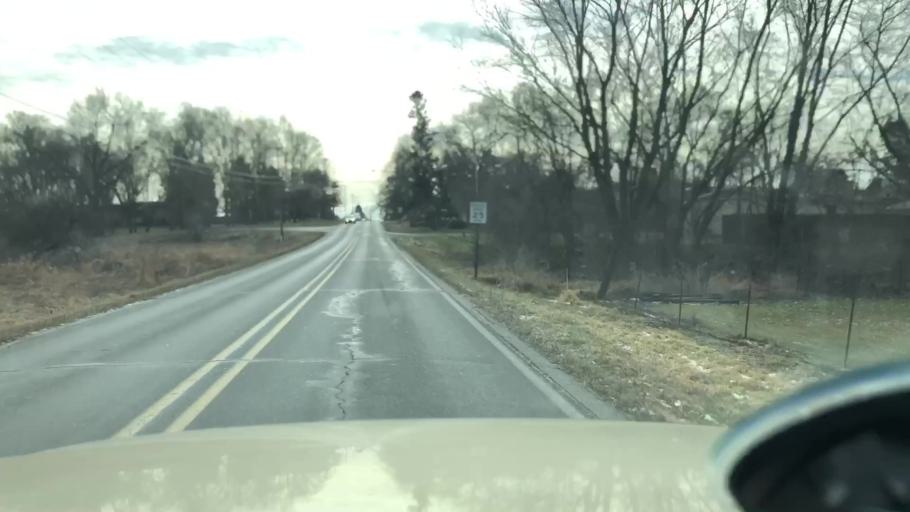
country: US
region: Michigan
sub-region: Jackson County
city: Jackson
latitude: 42.2632
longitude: -84.3650
